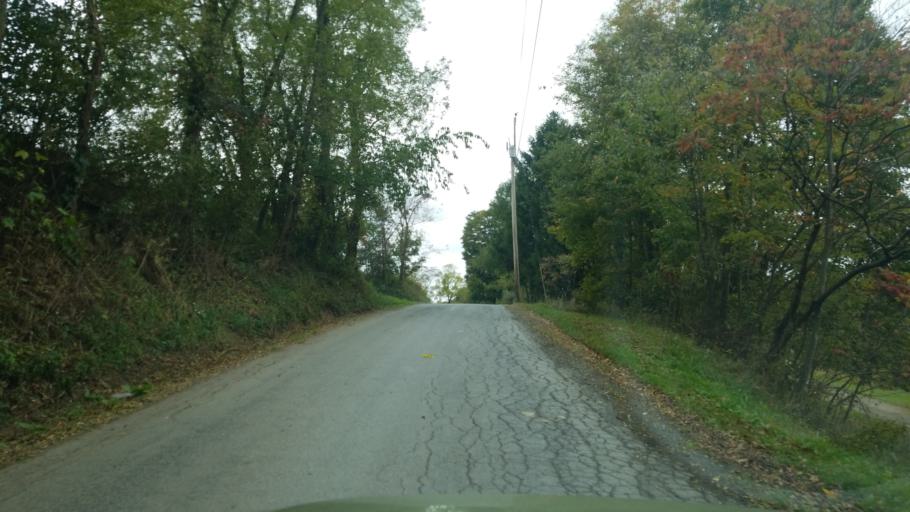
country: US
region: Pennsylvania
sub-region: Clearfield County
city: Curwensville
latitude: 40.9678
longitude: -78.5011
